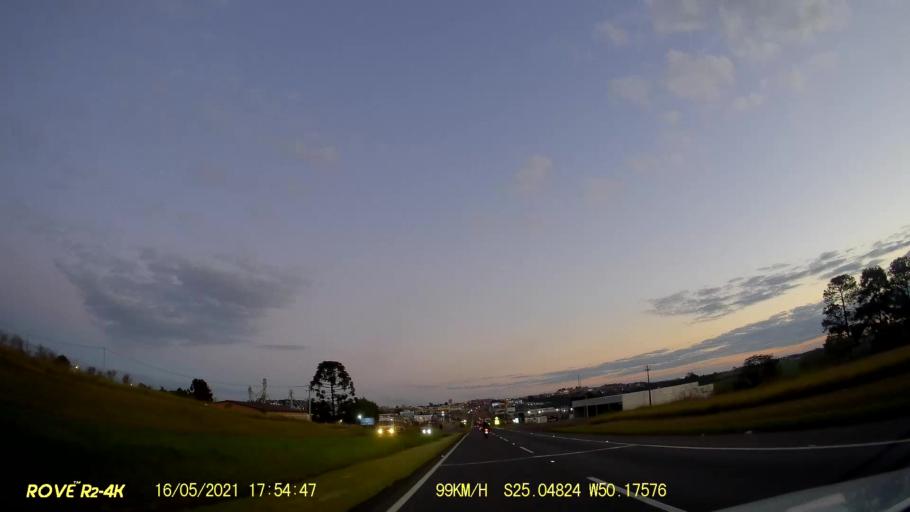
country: BR
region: Parana
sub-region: Ponta Grossa
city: Ponta Grossa
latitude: -25.0484
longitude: -50.1758
